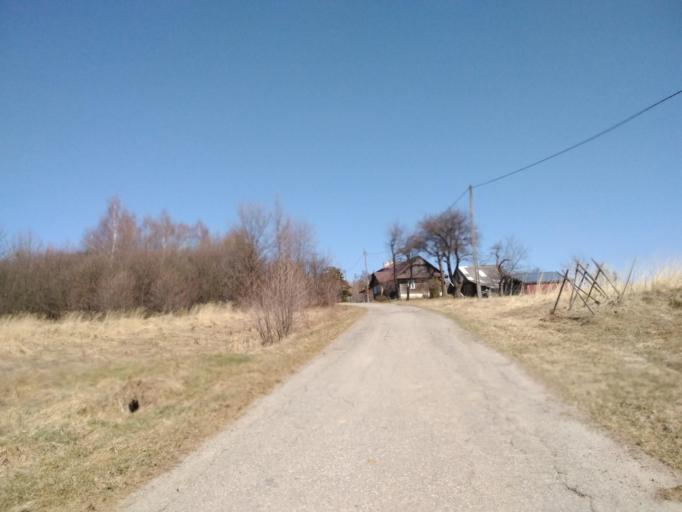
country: PL
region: Subcarpathian Voivodeship
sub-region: Powiat brzozowski
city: Jablonica Polska
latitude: 49.7418
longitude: 21.8938
